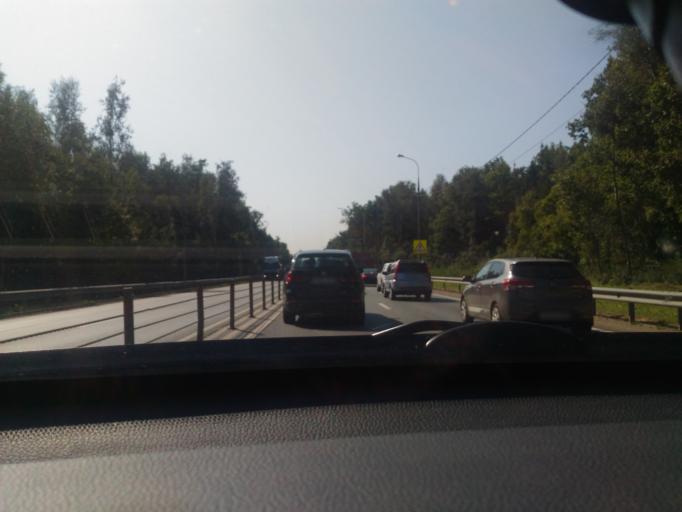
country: RU
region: Moskovskaya
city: Marfino
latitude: 56.0260
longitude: 37.5433
